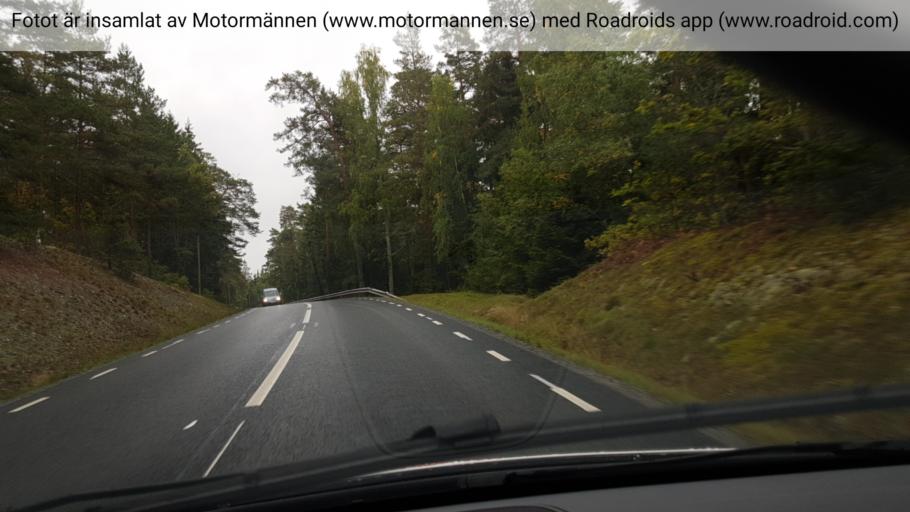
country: SE
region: Stockholm
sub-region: Nykvarns Kommun
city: Nykvarn
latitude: 59.1449
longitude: 17.4558
